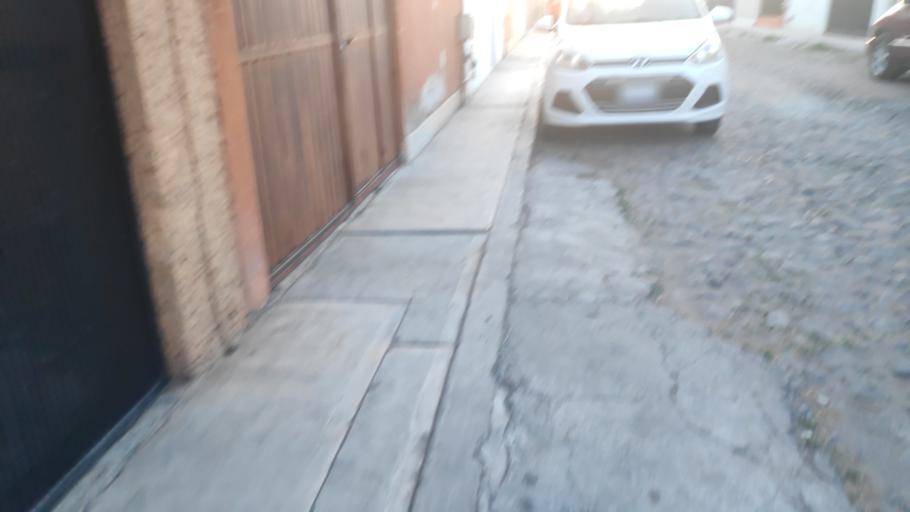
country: MX
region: Queretaro
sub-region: Queretaro
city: Santiago de Queretaro
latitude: 20.5811
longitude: -100.3706
